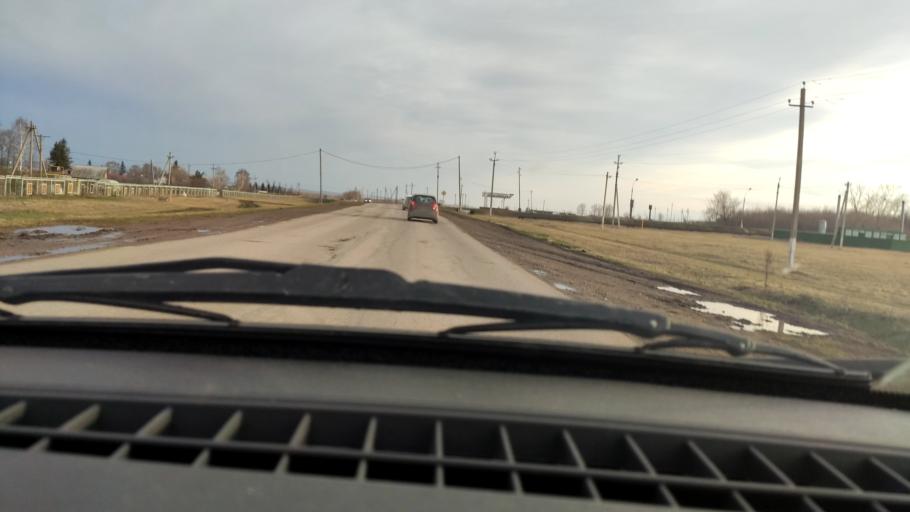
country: RU
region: Bashkortostan
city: Davlekanovo
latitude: 54.3827
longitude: 55.1962
